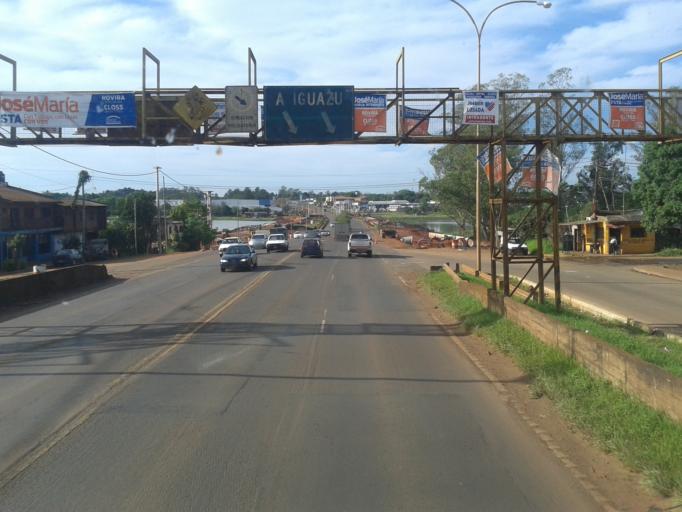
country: AR
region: Misiones
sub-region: Departamento de Capital
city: Posadas
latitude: -27.4159
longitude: -55.9007
